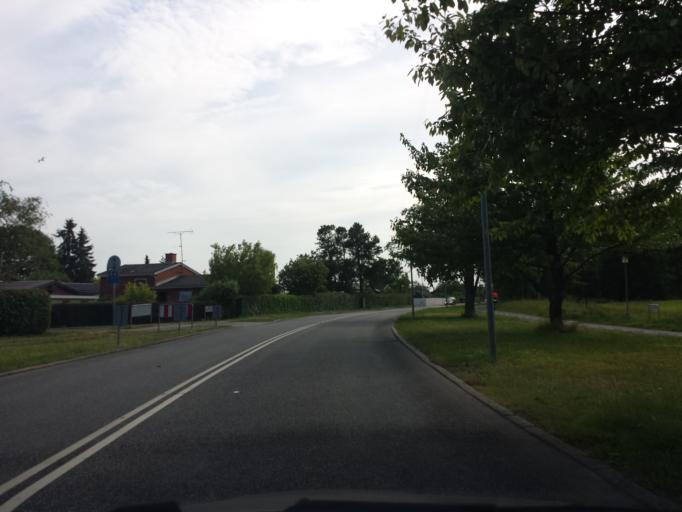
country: DK
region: Capital Region
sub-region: Ballerup Kommune
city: Ballerup
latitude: 55.7183
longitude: 12.3915
